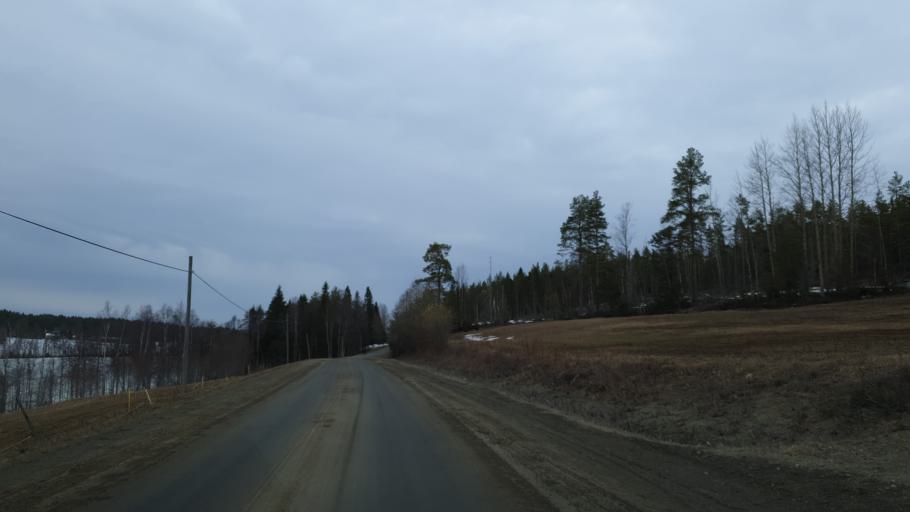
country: SE
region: Vaesterbotten
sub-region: Skelleftea Kommun
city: Burea
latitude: 64.3189
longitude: 21.1392
